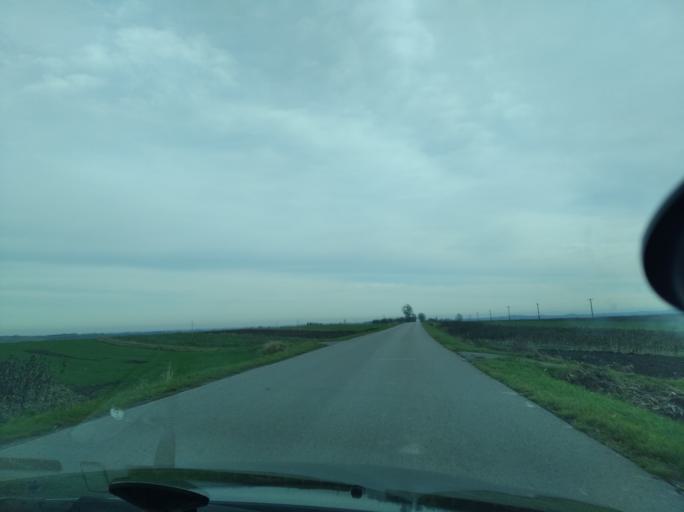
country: PL
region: Subcarpathian Voivodeship
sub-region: Powiat przeworski
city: Nowosielce
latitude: 50.0353
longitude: 22.4080
